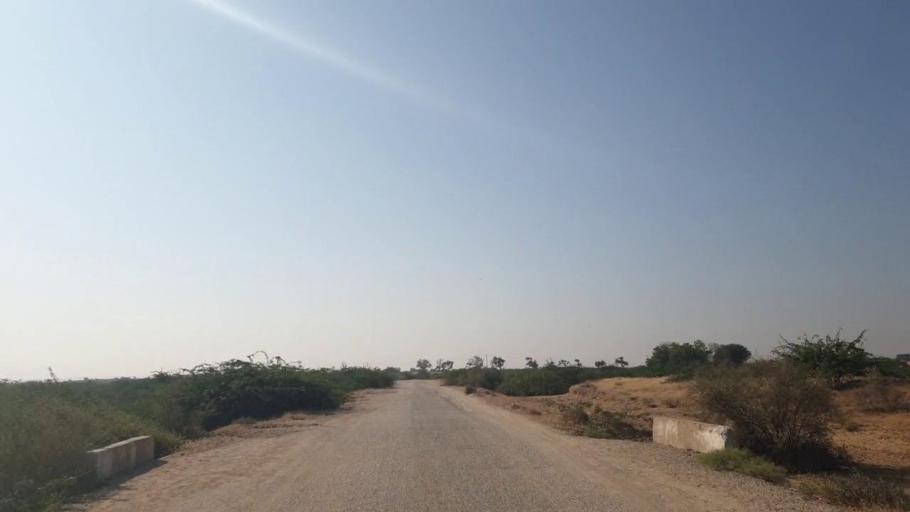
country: PK
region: Sindh
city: Thatta
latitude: 25.1408
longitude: 67.7722
